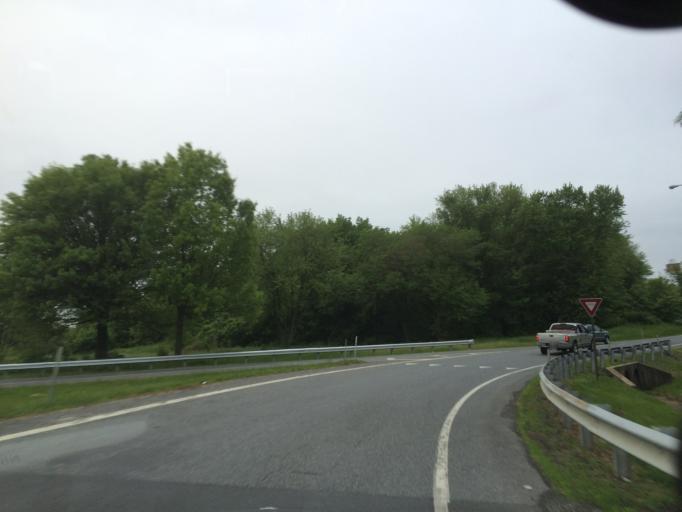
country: US
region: Maryland
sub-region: Washington County
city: Halfway
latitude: 39.6076
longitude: -77.7293
